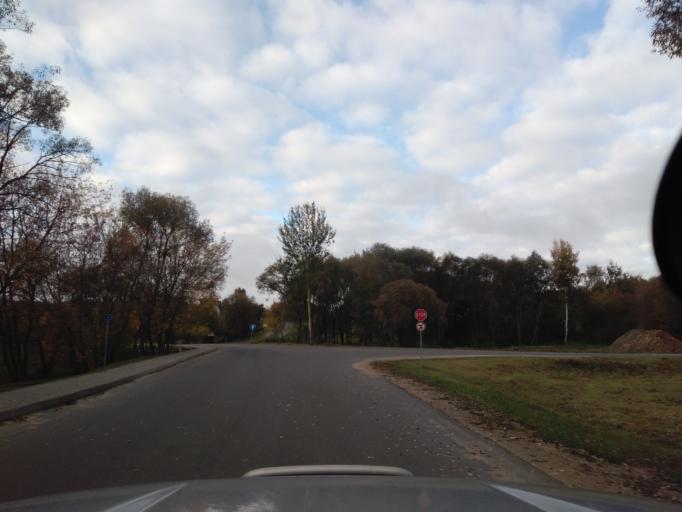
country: BY
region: Minsk
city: Kapyl'
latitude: 53.1581
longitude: 27.0893
